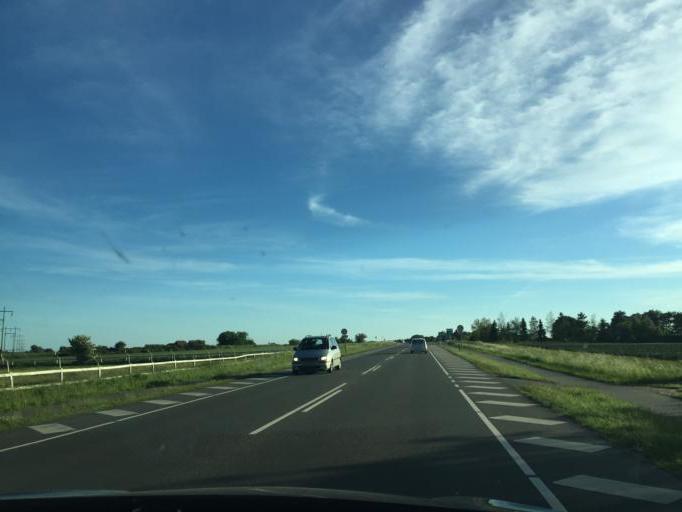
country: DK
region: Zealand
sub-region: Slagelse Kommune
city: Forlev
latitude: 55.3685
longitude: 11.2786
